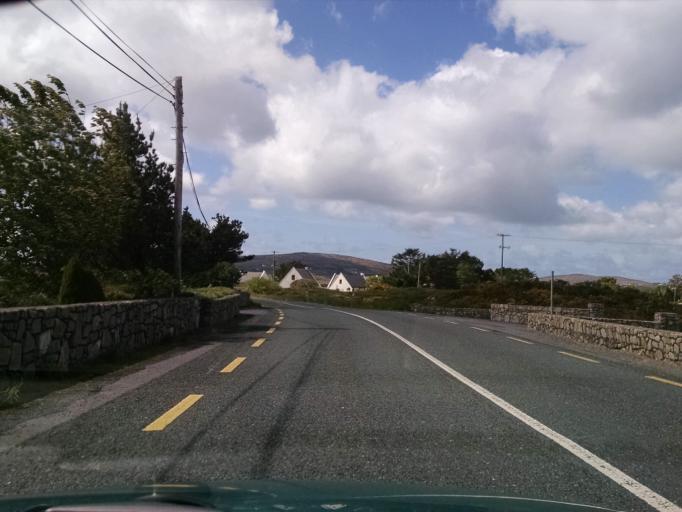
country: IE
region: Connaught
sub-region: County Galway
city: Oughterard
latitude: 53.3095
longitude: -9.6310
